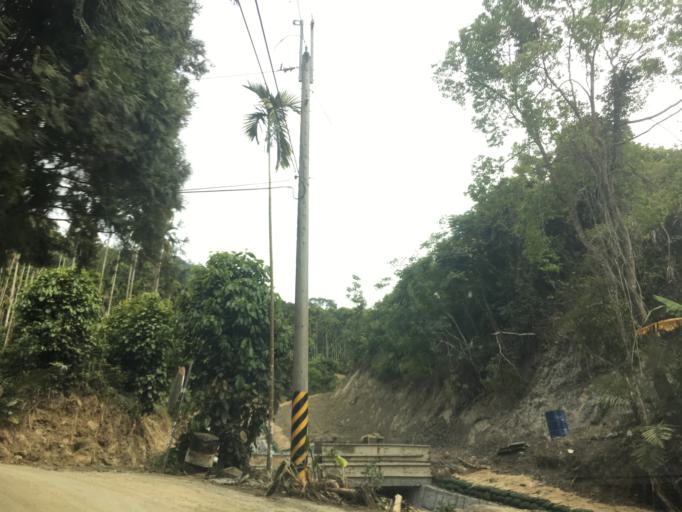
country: TW
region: Taiwan
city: Zhongxing New Village
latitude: 23.9760
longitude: 120.8204
